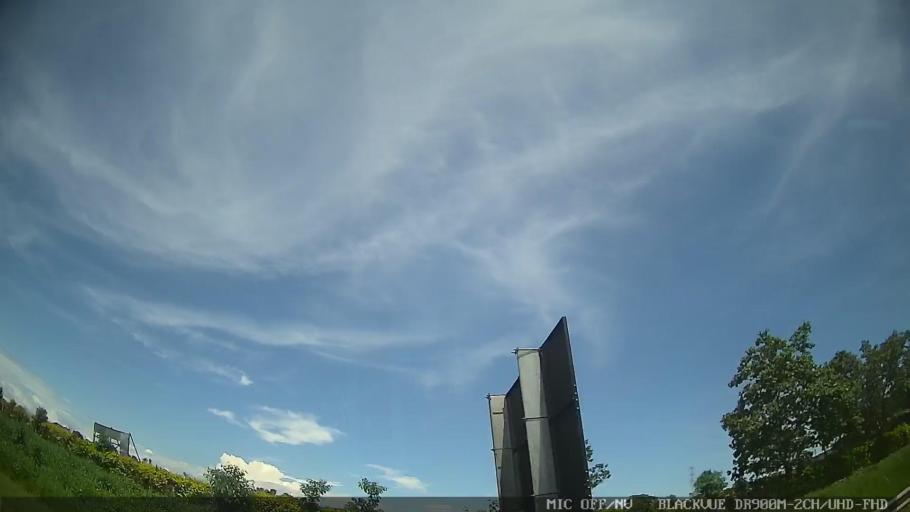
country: BR
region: Sao Paulo
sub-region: Jaguariuna
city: Jaguariuna
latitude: -22.6747
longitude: -47.0033
